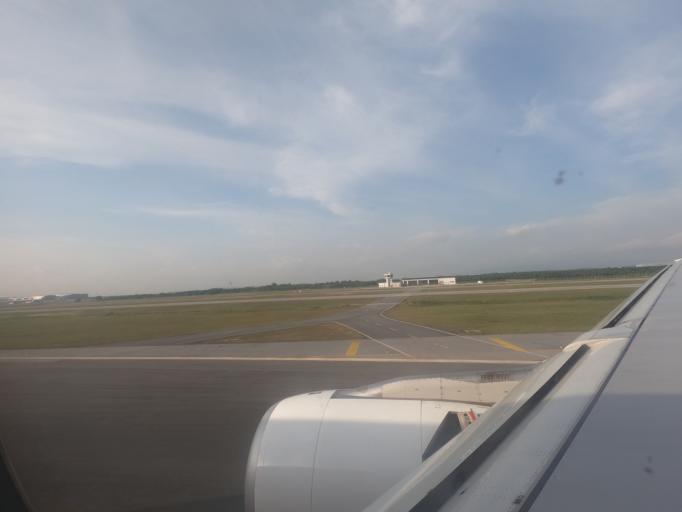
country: MY
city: Sungai Pelek New Village
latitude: 2.7222
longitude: 101.6882
